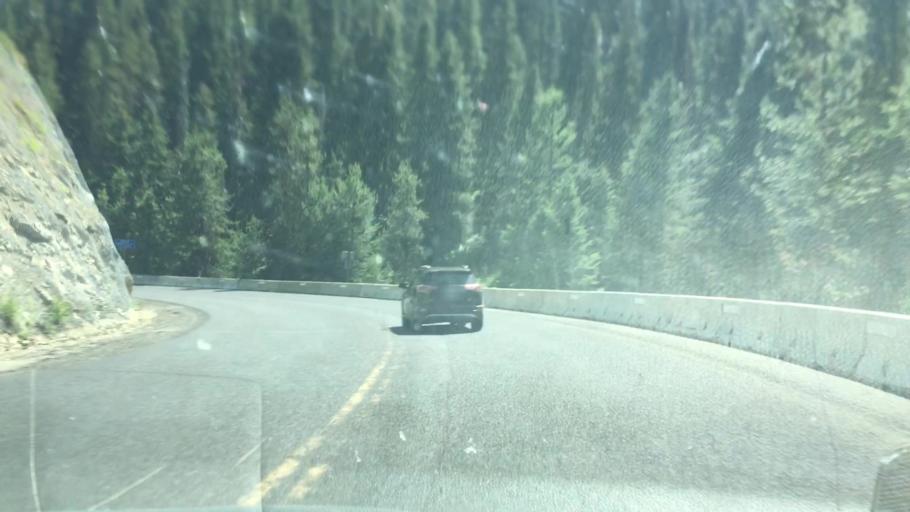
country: US
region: Idaho
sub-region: Valley County
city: McCall
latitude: 44.9617
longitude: -116.1739
